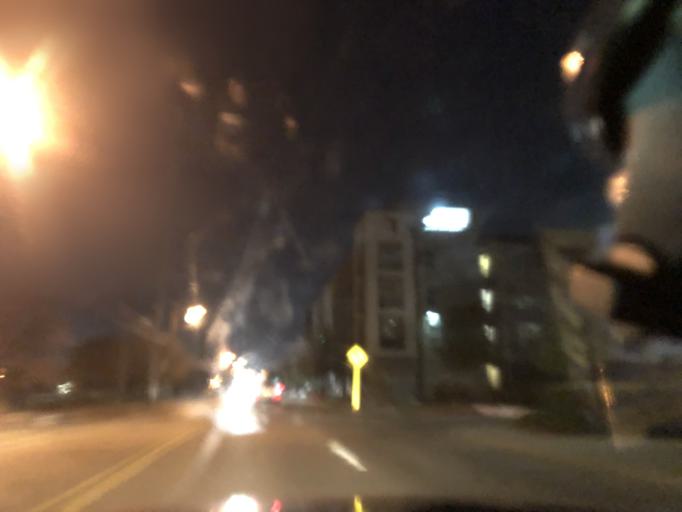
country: US
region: Texas
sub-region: Dallas County
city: University Park
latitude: 32.8241
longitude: -96.8398
